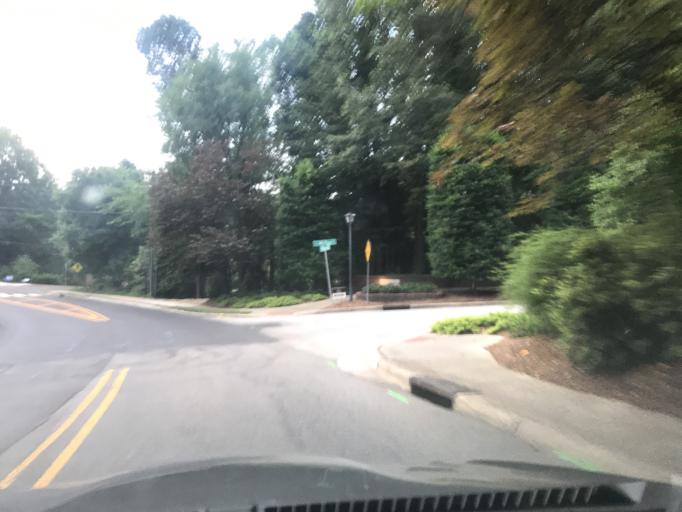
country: US
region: North Carolina
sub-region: Orange County
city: Chapel Hill
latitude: 35.9224
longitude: -79.0515
